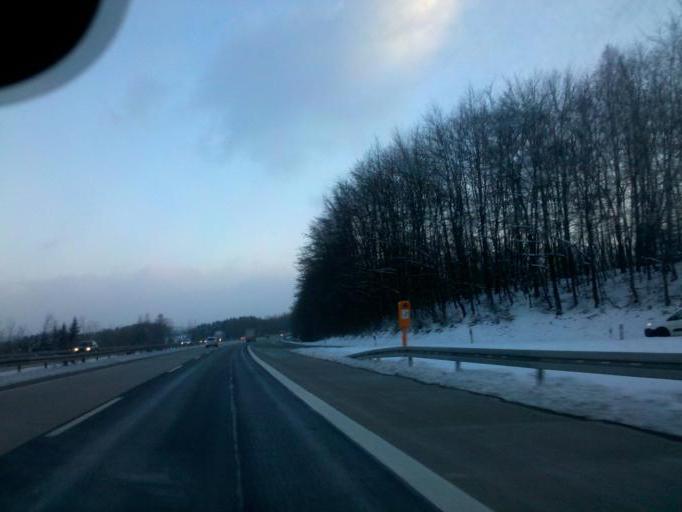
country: DE
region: North Rhine-Westphalia
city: Freudenberg
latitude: 50.9089
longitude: 7.9136
